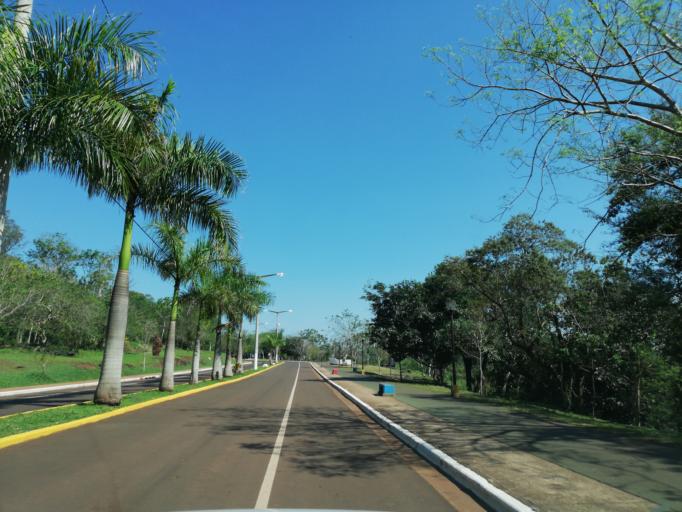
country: AR
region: Misiones
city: Puerto Eldorado
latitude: -26.4086
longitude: -54.6909
